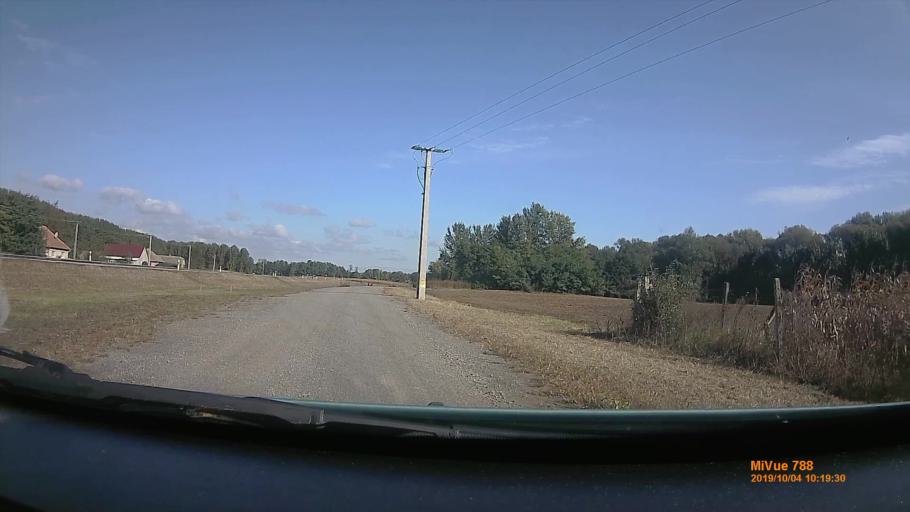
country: HU
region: Szabolcs-Szatmar-Bereg
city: Nyirtelek
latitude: 47.9619
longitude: 21.6571
